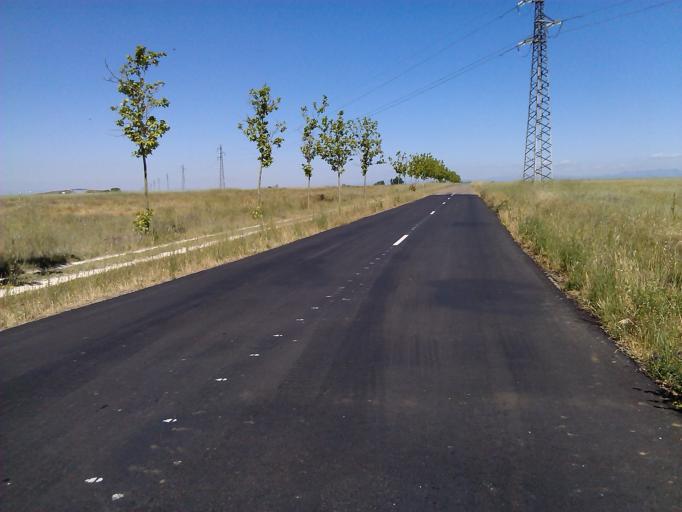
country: ES
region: Castille and Leon
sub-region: Provincia de Leon
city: Vallecillo
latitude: 42.4271
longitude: -5.2289
